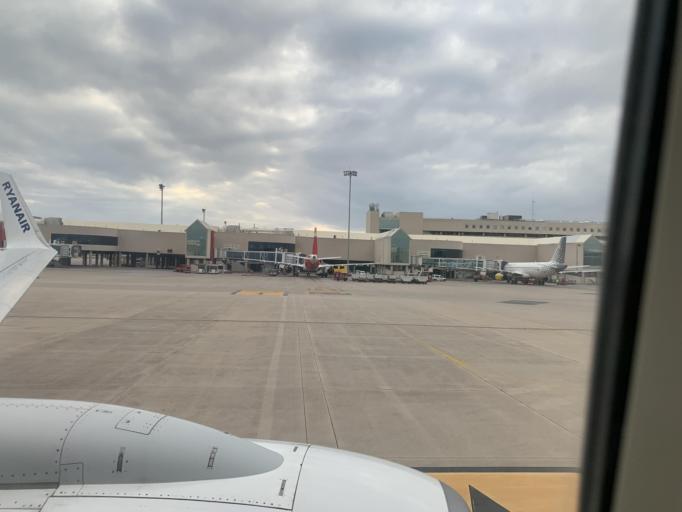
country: ES
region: Balearic Islands
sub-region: Illes Balears
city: s'Arenal
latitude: 39.5476
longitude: 2.7354
